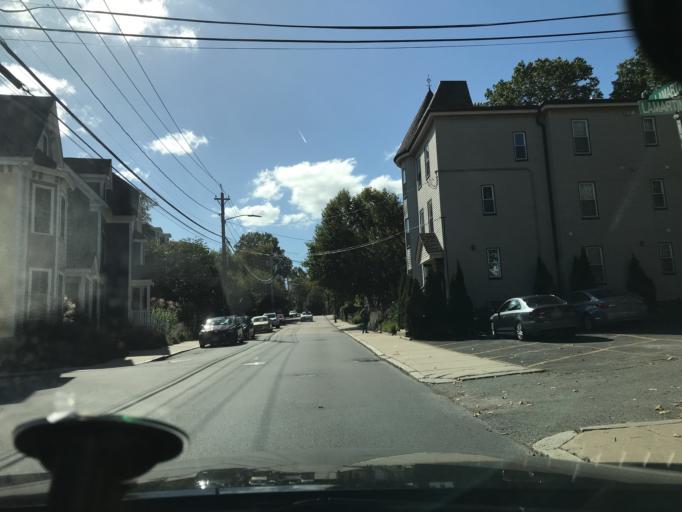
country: US
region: Massachusetts
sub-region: Suffolk County
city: Jamaica Plain
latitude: 42.3141
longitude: -71.1068
